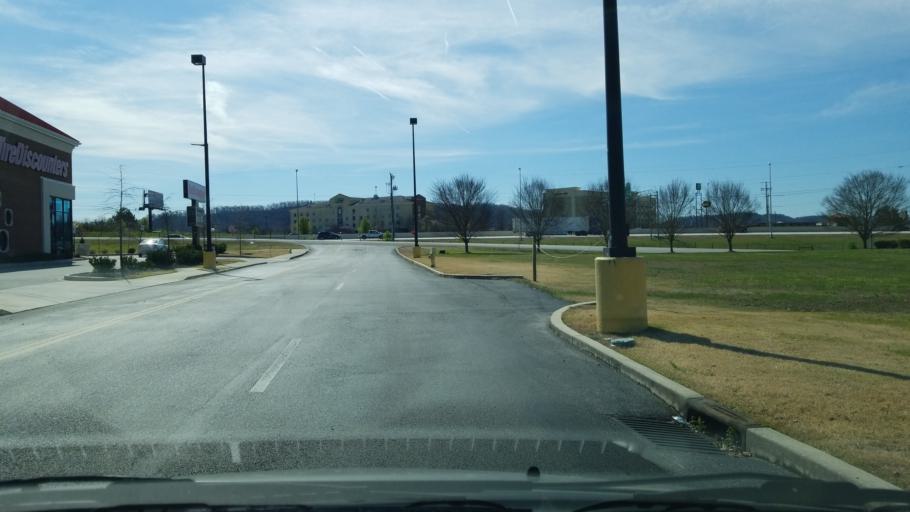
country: US
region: Tennessee
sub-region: Hamilton County
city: Collegedale
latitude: 35.0892
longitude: -85.0648
